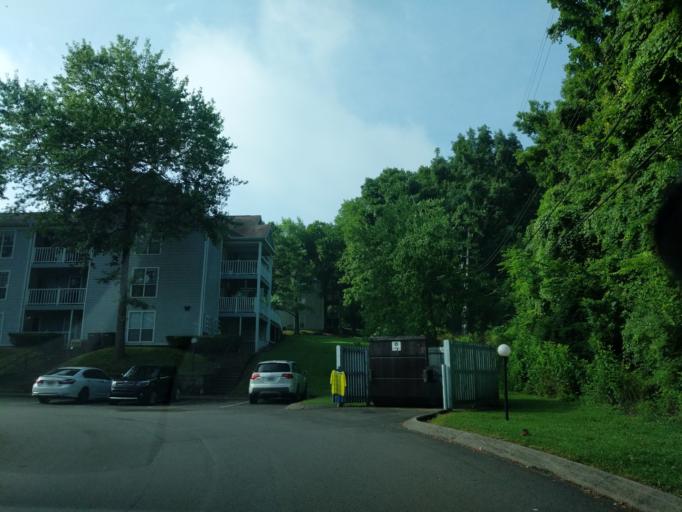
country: US
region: Tennessee
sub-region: Davidson County
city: Goodlettsville
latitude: 36.3136
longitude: -86.6974
